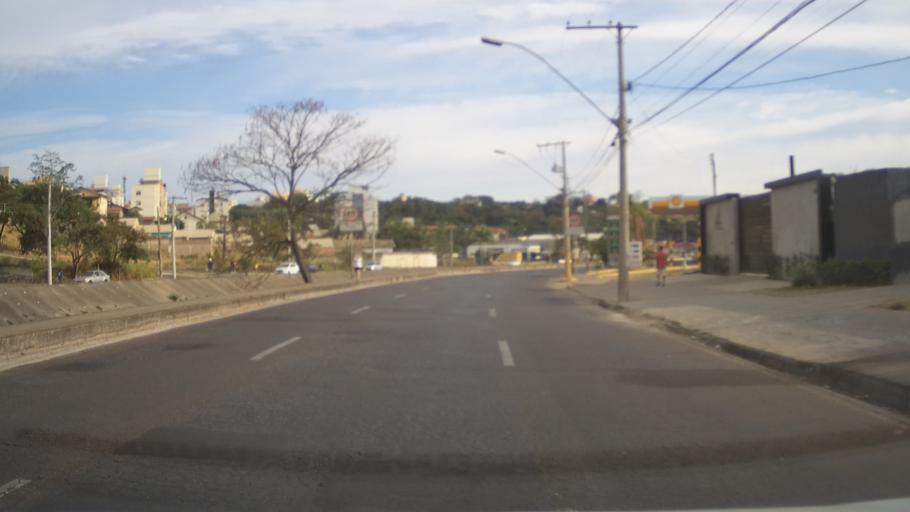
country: BR
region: Minas Gerais
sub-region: Contagem
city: Contagem
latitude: -19.8800
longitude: -44.0057
